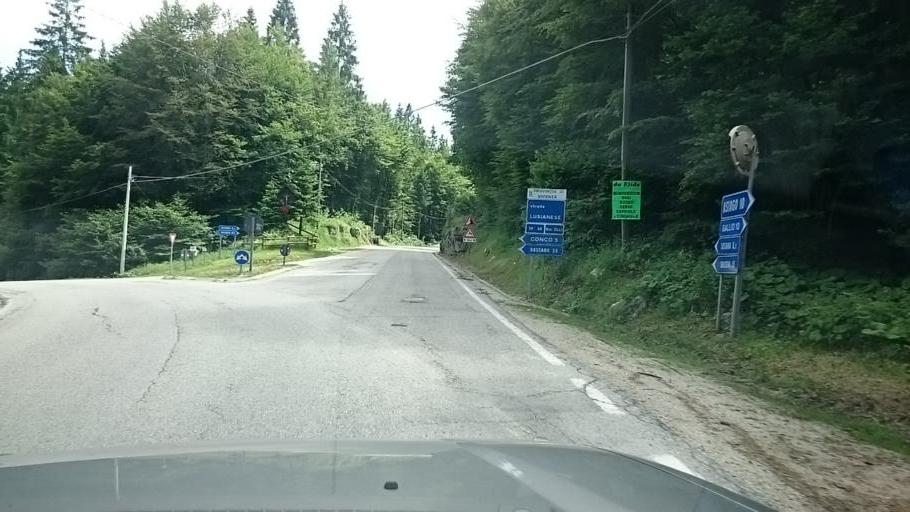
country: IT
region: Veneto
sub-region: Provincia di Vicenza
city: Conco
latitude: 45.8274
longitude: 11.5984
